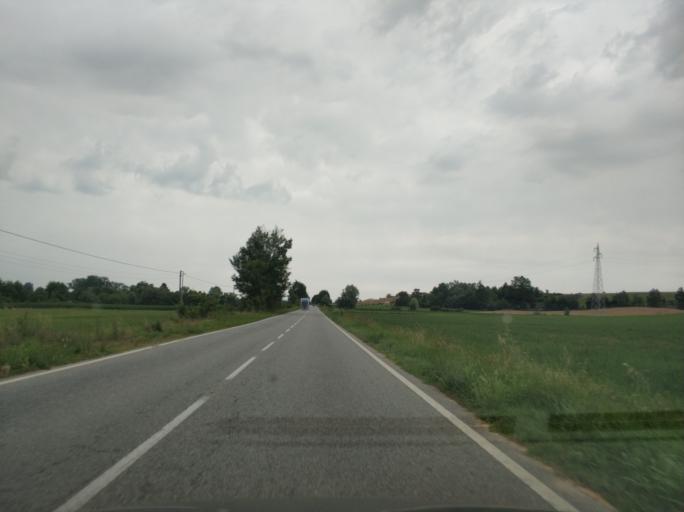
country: IT
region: Piedmont
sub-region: Provincia di Torino
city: Pralormo
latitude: 44.8386
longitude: 7.9145
